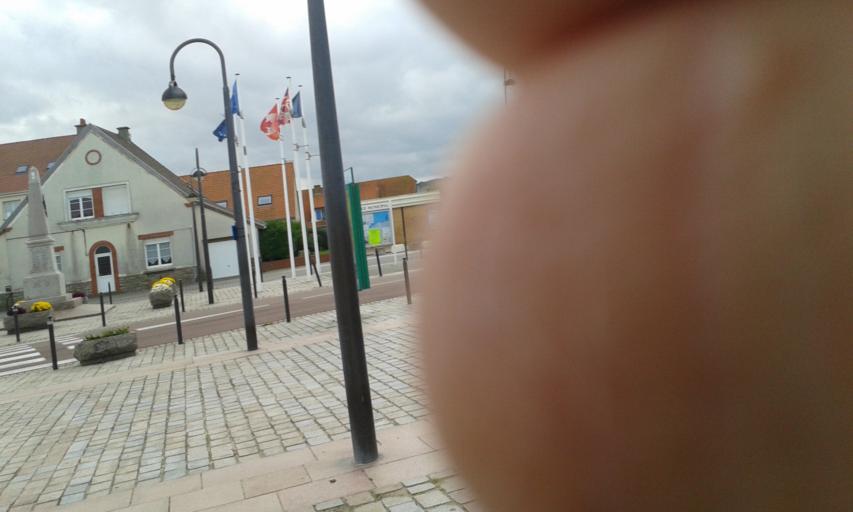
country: FR
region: Nord-Pas-de-Calais
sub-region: Departement du Pas-de-Calais
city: Sangatte
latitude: 50.9475
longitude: 1.7581
